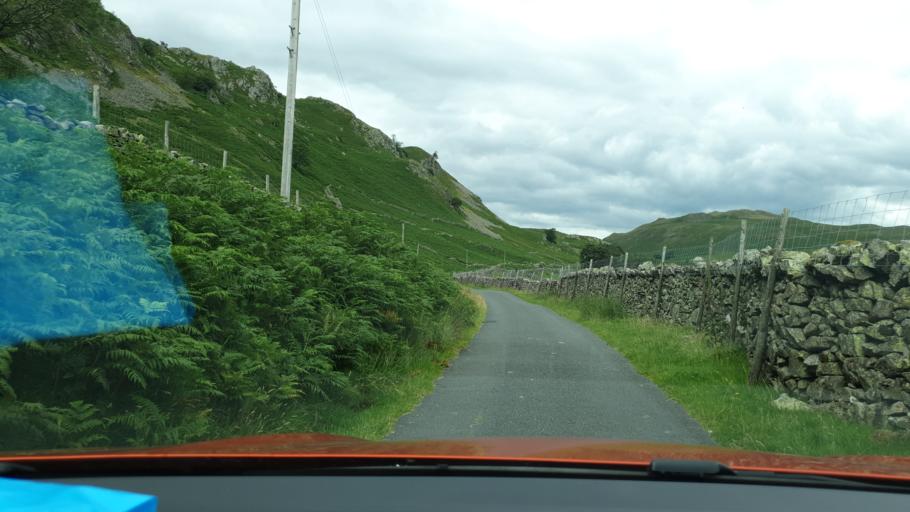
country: GB
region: England
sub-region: Cumbria
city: Ambleside
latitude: 54.5527
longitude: -2.8779
